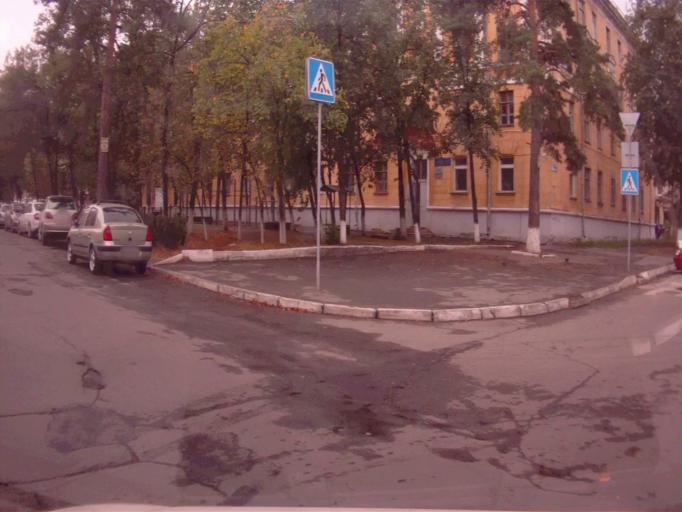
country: RU
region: Chelyabinsk
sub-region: Gorod Chelyabinsk
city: Chelyabinsk
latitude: 55.1604
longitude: 61.3680
